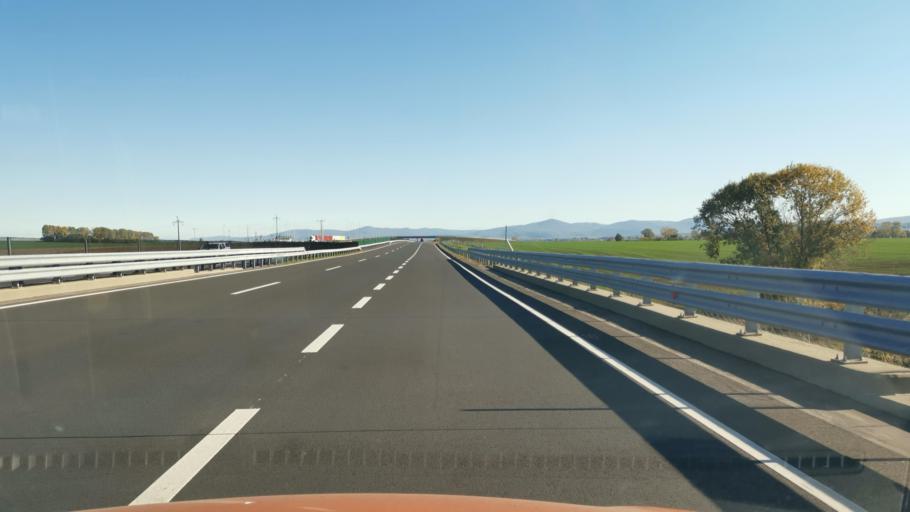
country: HU
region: Borsod-Abauj-Zemplen
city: Halmaj
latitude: 48.2912
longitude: 21.0313
